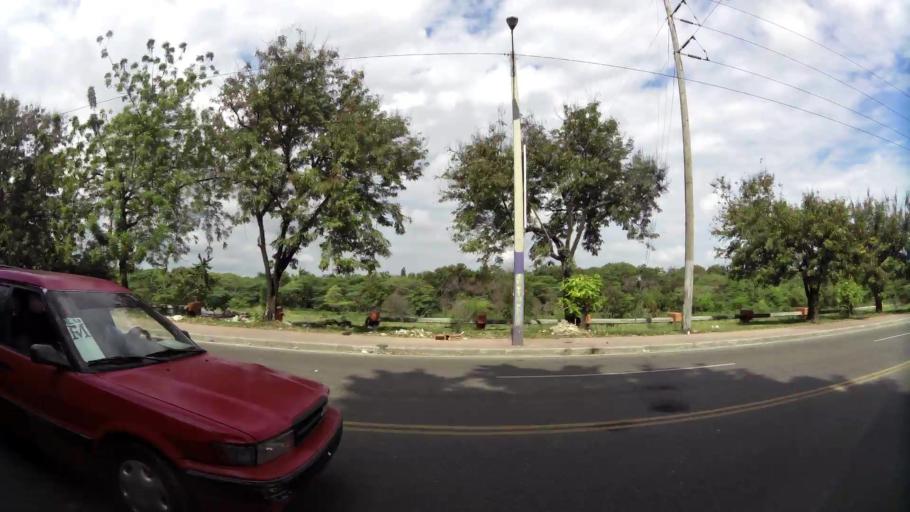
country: DO
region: Santiago
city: Santiago de los Caballeros
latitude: 19.4589
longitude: -70.7146
